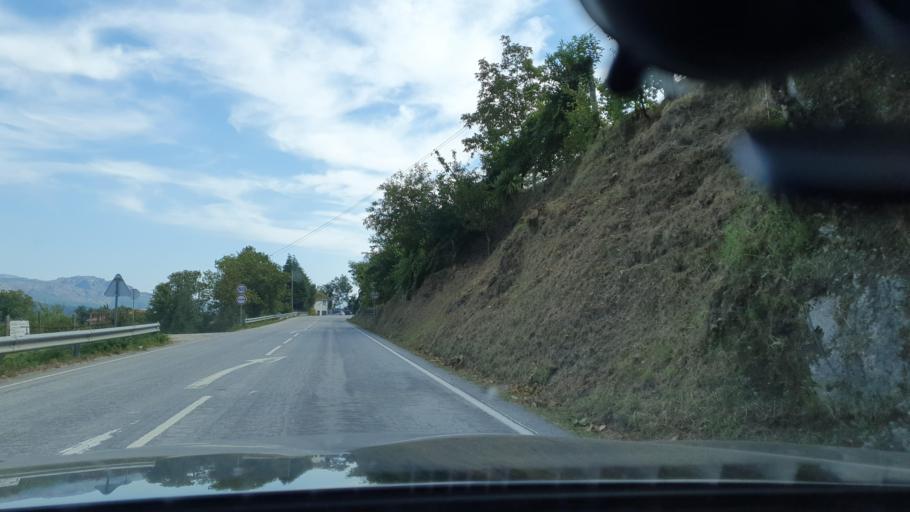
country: PT
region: Braga
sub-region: Vieira do Minho
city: Vieira do Minho
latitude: 41.6782
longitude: -8.1254
